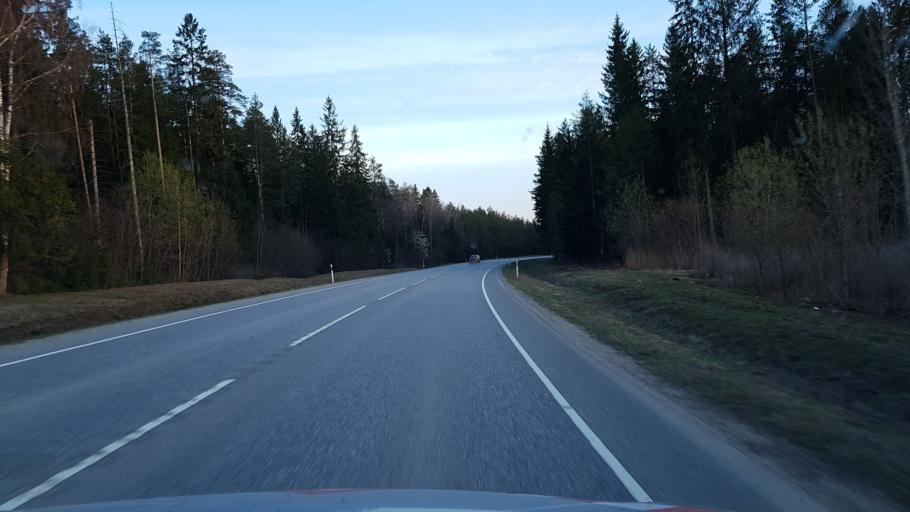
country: EE
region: Laeaene-Virumaa
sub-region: Someru vald
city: Someru
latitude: 59.3404
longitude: 26.4118
